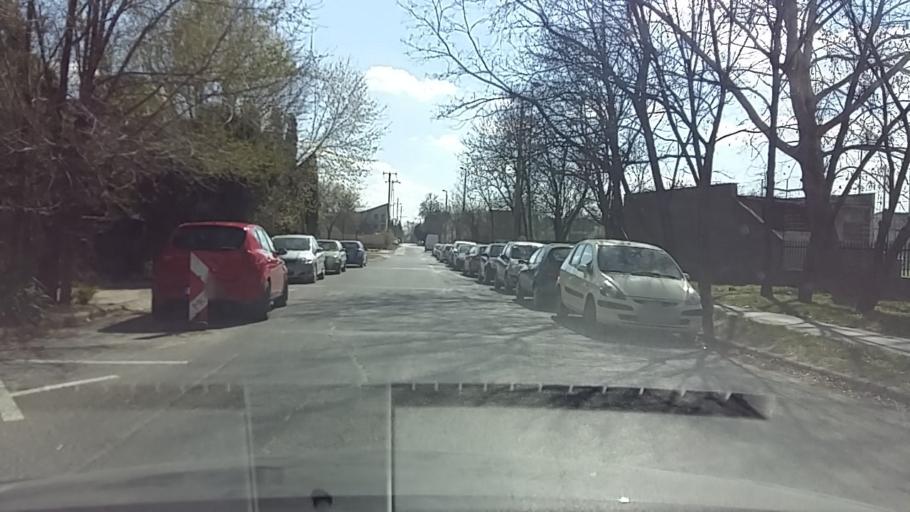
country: HU
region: Pest
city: Szigetszentmiklos
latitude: 47.3438
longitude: 19.0431
